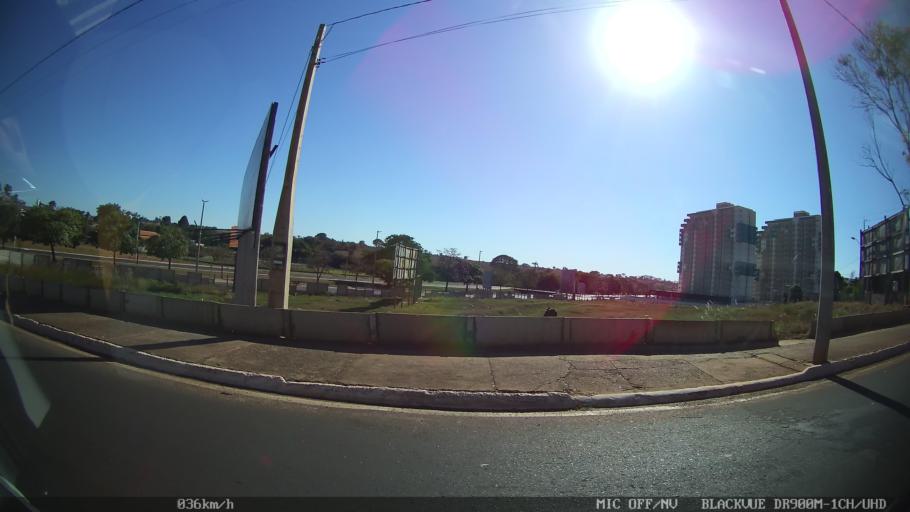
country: BR
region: Sao Paulo
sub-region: Olimpia
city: Olimpia
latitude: -20.7279
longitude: -48.9142
